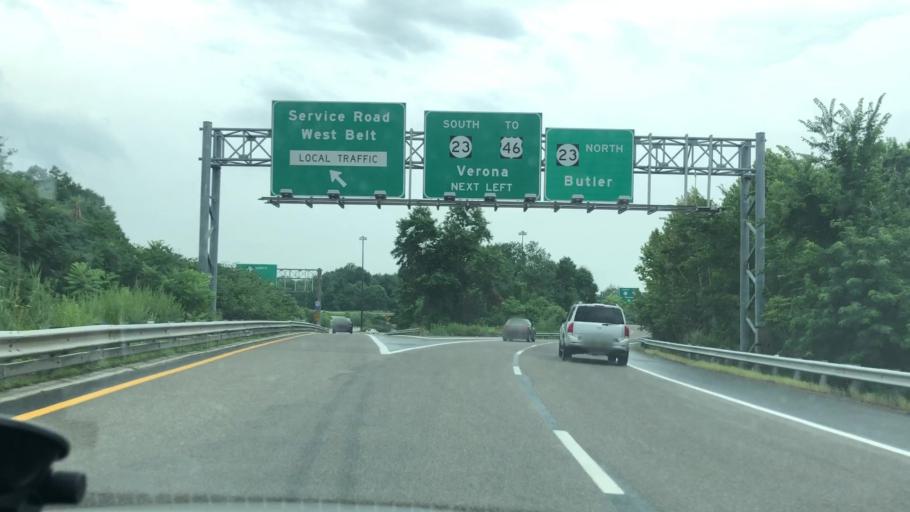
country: US
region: New Jersey
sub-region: Passaic County
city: Singac
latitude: 40.8979
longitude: -74.2502
